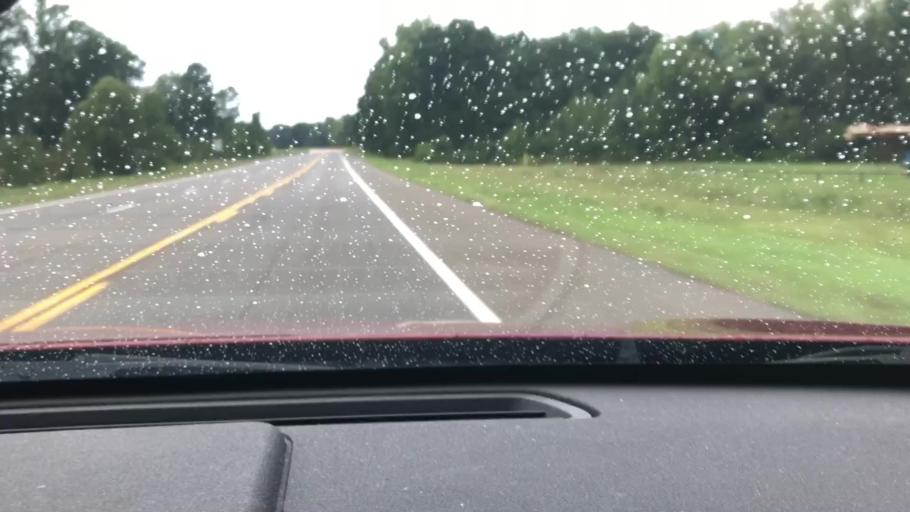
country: US
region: Arkansas
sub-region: Lafayette County
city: Stamps
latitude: 33.3638
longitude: -93.4697
